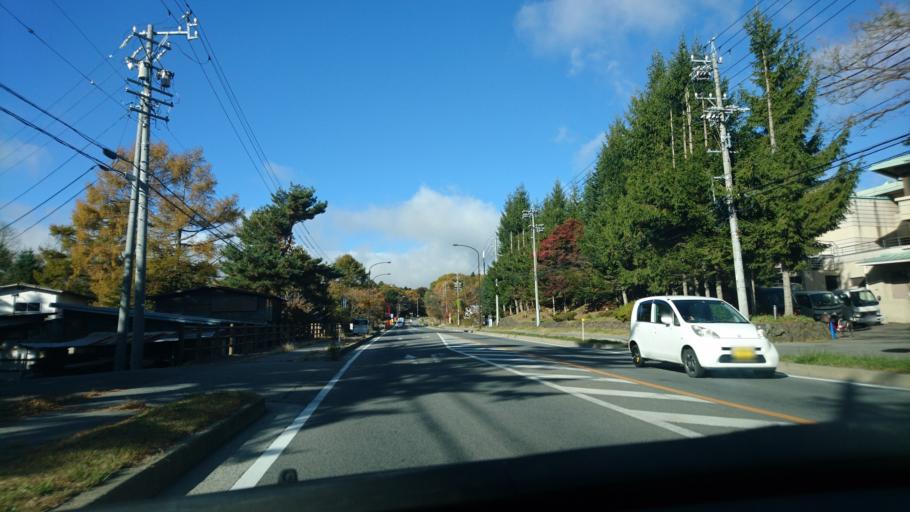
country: JP
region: Nagano
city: Komoro
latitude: 36.3392
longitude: 138.5780
